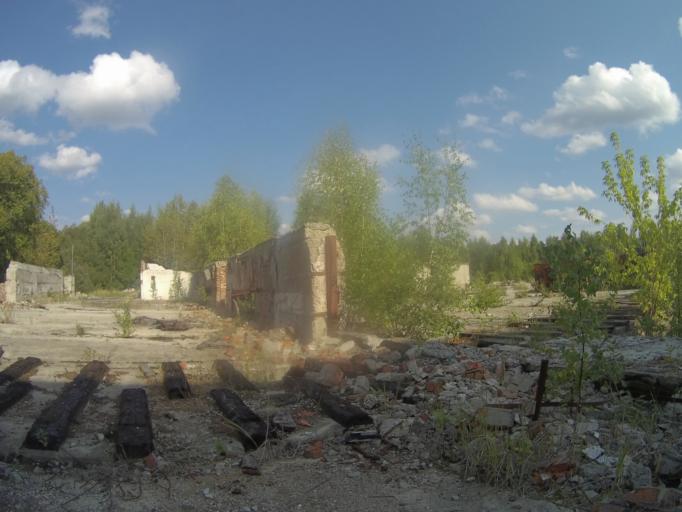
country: RU
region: Vladimir
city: Raduzhnyy
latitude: 55.9777
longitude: 40.2683
